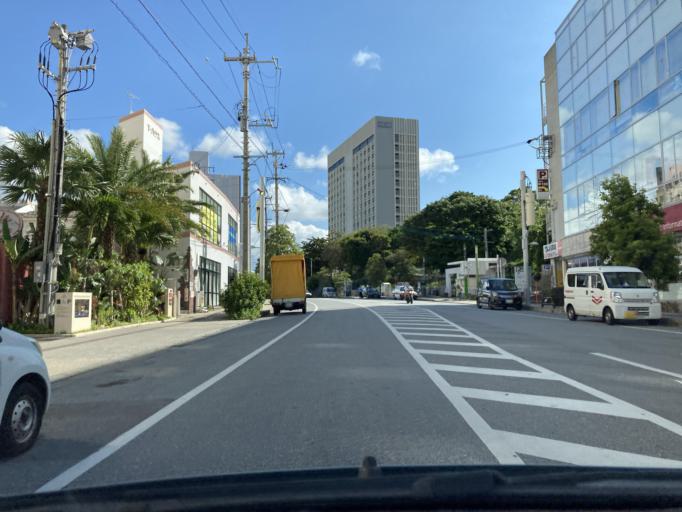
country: JP
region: Okinawa
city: Naha-shi
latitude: 26.2165
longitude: 127.6896
